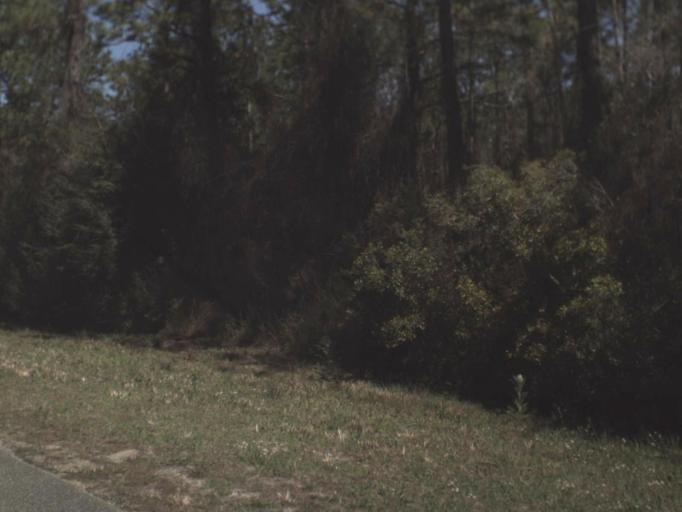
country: US
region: Florida
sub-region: Gulf County
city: Port Saint Joe
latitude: 29.7666
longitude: -85.2622
